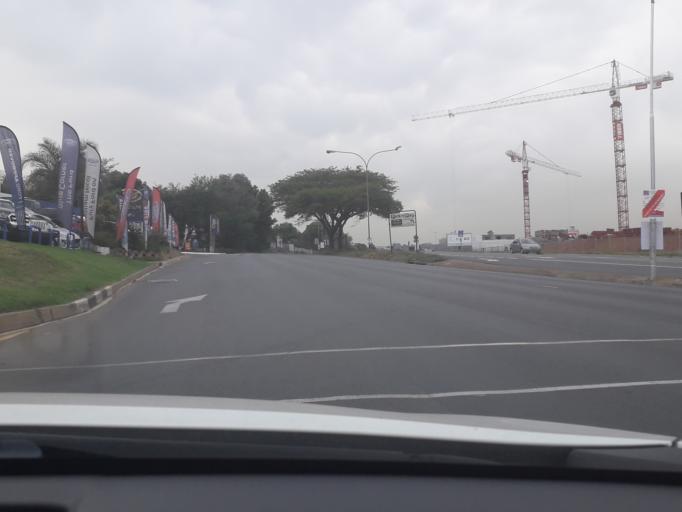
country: ZA
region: Gauteng
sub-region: City of Johannesburg Metropolitan Municipality
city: Johannesburg
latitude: -26.0928
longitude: 28.0292
